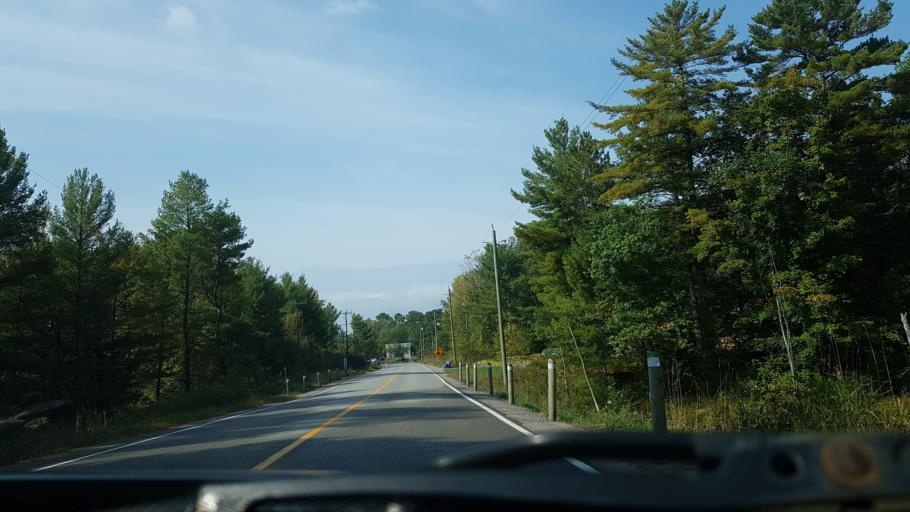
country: CA
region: Ontario
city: Gravenhurst
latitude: 44.7655
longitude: -79.3268
